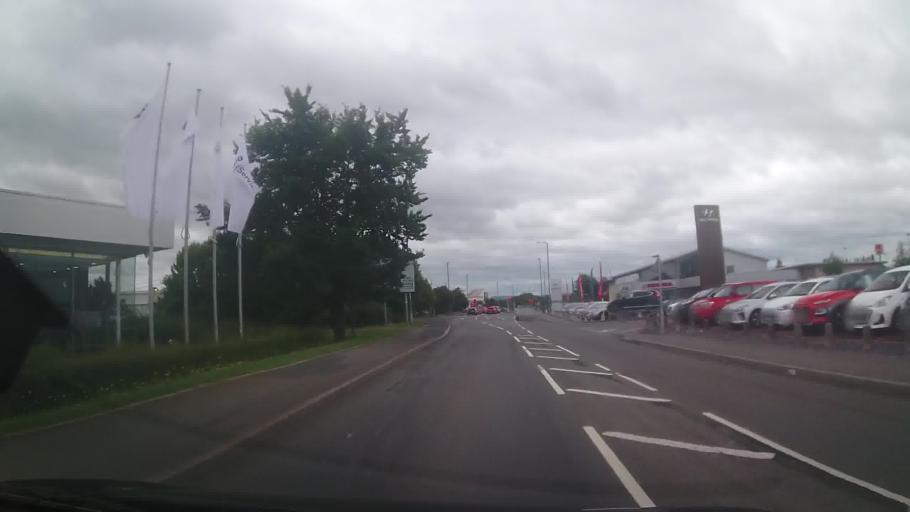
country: GB
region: England
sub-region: Shropshire
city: Astley
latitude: 52.7401
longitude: -2.7209
